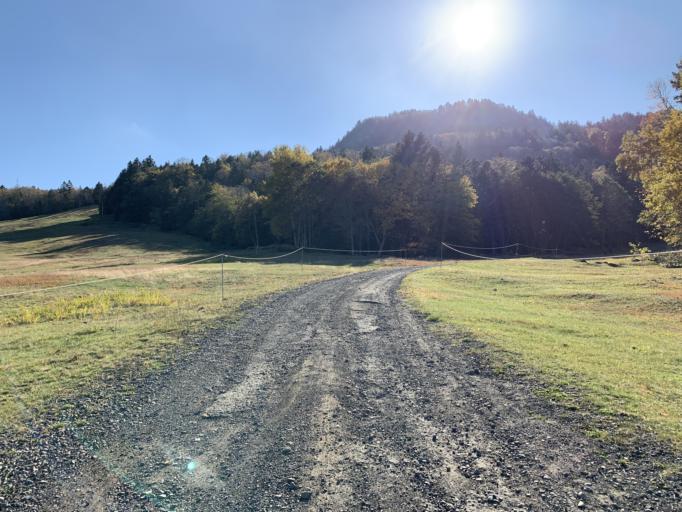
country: JP
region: Hokkaido
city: Bihoro
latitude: 43.4233
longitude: 144.0841
